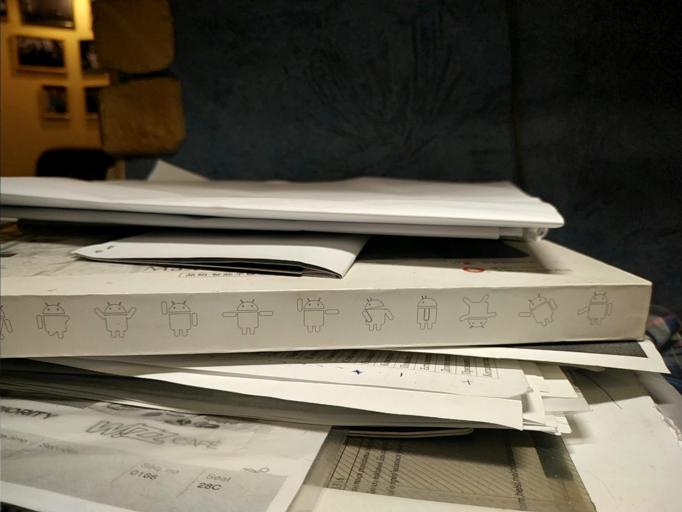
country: RU
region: Tverskaya
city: Zubtsov
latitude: 56.0792
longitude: 34.8084
